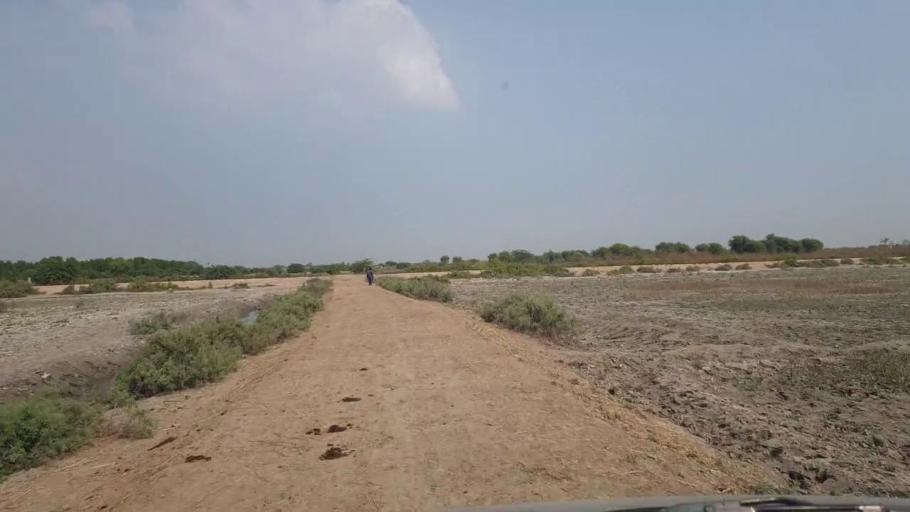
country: PK
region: Sindh
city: Matli
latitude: 24.9922
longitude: 68.7211
